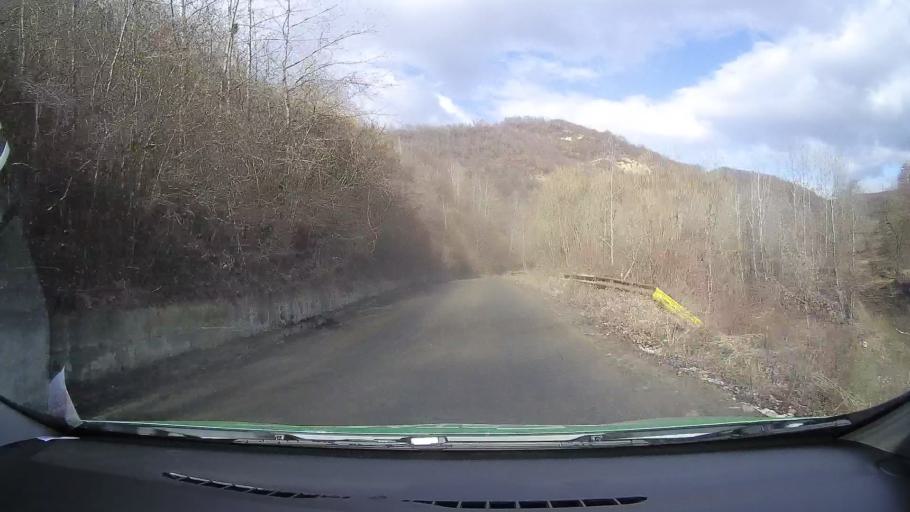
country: RO
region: Dambovita
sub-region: Oras Pucioasa
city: Pucioasa
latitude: 45.1006
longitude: 25.4417
